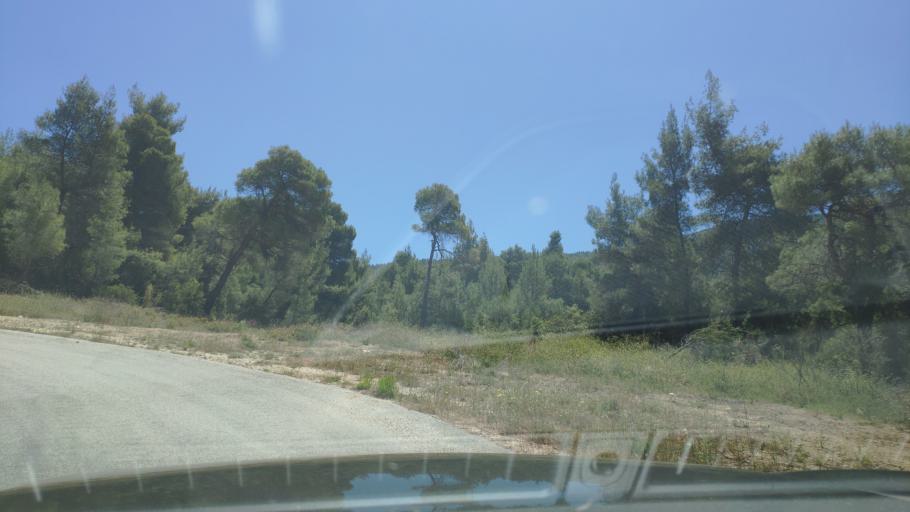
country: GR
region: Peloponnese
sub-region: Nomos Korinthias
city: Khiliomodhi
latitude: 37.8013
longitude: 22.8950
